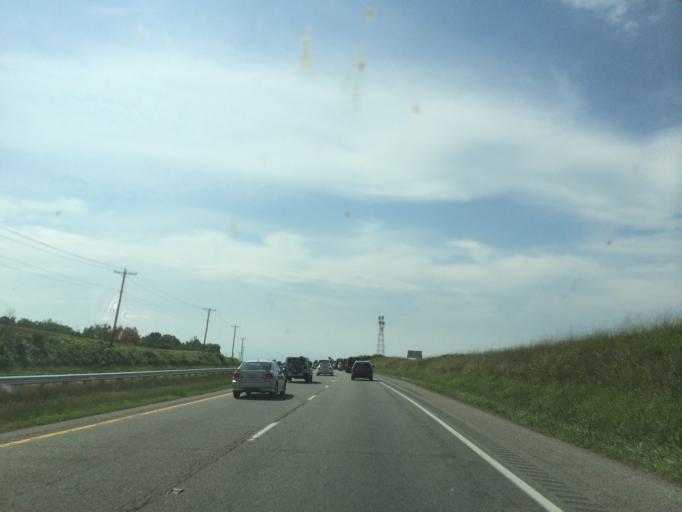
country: US
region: Maryland
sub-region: Queen Anne's County
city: Centreville
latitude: 38.9512
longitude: -76.0687
